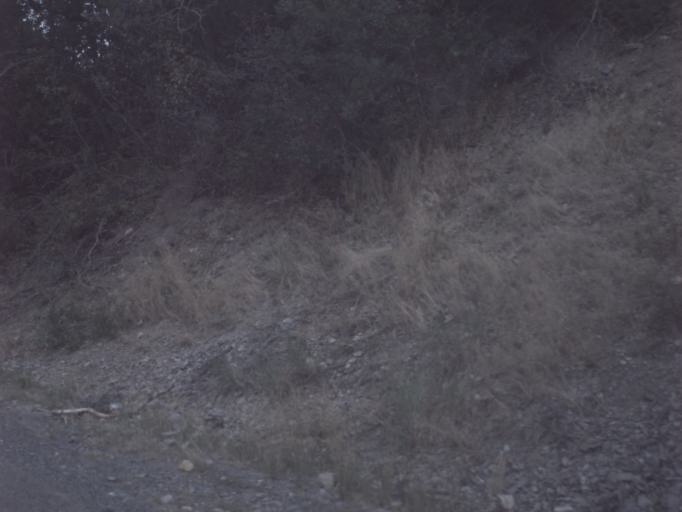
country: US
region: Utah
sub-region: Utah County
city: Cedar Hills
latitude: 40.4507
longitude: -111.6445
